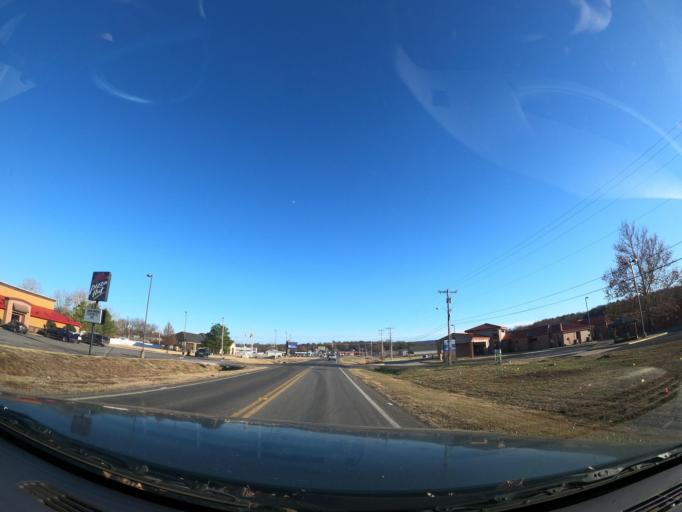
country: US
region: Oklahoma
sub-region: Latimer County
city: Wilburton
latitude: 34.9201
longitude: -95.3204
